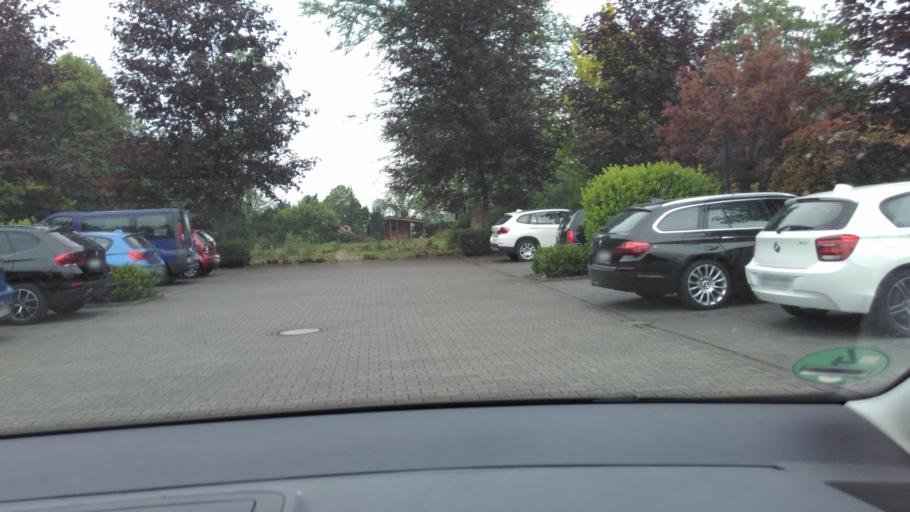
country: DE
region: North Rhine-Westphalia
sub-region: Regierungsbezirk Detmold
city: Verl
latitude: 51.8793
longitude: 8.4700
